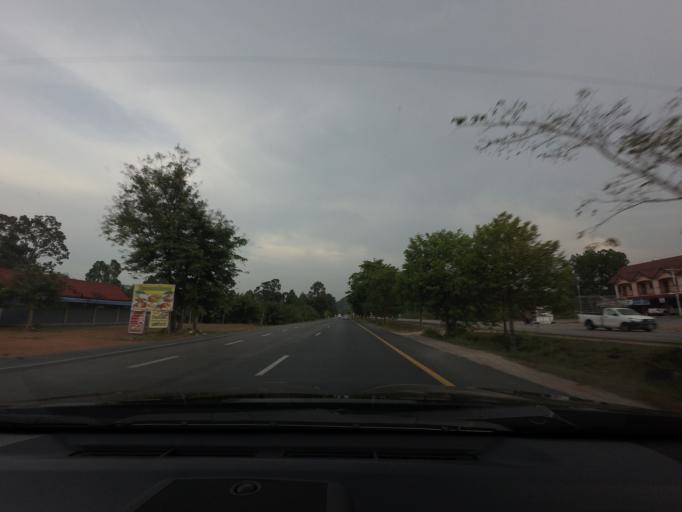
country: TH
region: Surat Thani
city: Tha Chana
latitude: 9.4994
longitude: 99.1329
